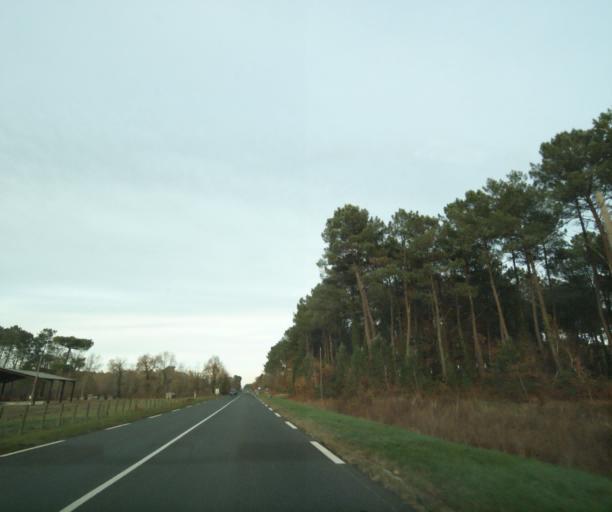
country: FR
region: Aquitaine
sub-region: Departement de la Gironde
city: Bazas
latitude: 44.3089
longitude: -0.2511
